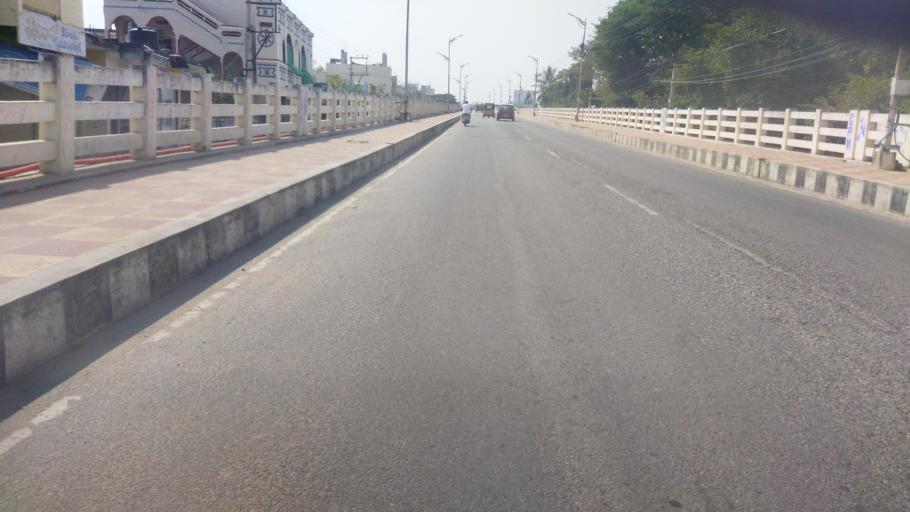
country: IN
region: Telangana
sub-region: Nalgonda
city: Nalgonda
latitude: 17.0677
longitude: 79.2814
